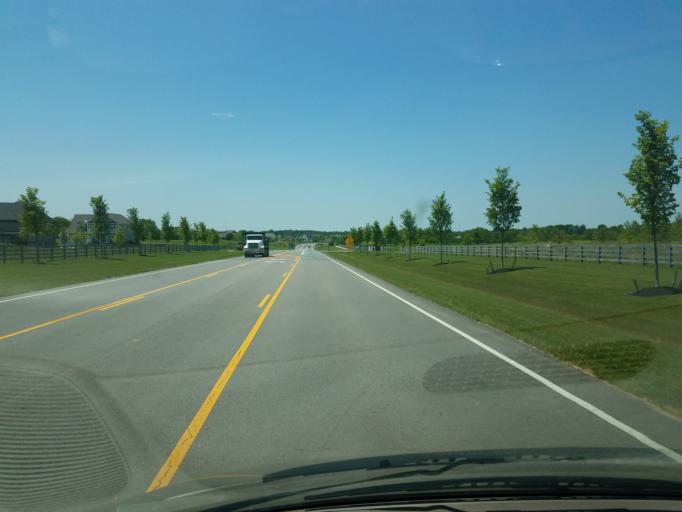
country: US
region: Ohio
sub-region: Delaware County
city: Sunbury
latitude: 40.2841
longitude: -82.8926
